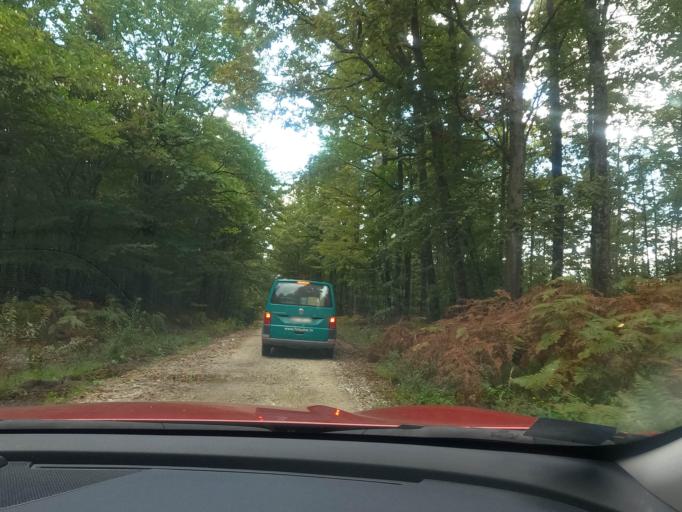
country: BA
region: Federation of Bosnia and Herzegovina
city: Velika Kladusa
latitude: 45.2506
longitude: 15.7931
